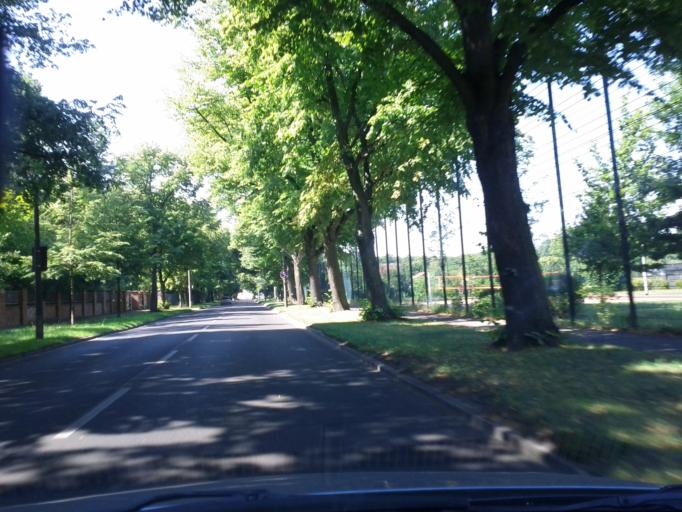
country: DE
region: Berlin
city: Weissensee
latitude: 52.5568
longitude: 13.4505
